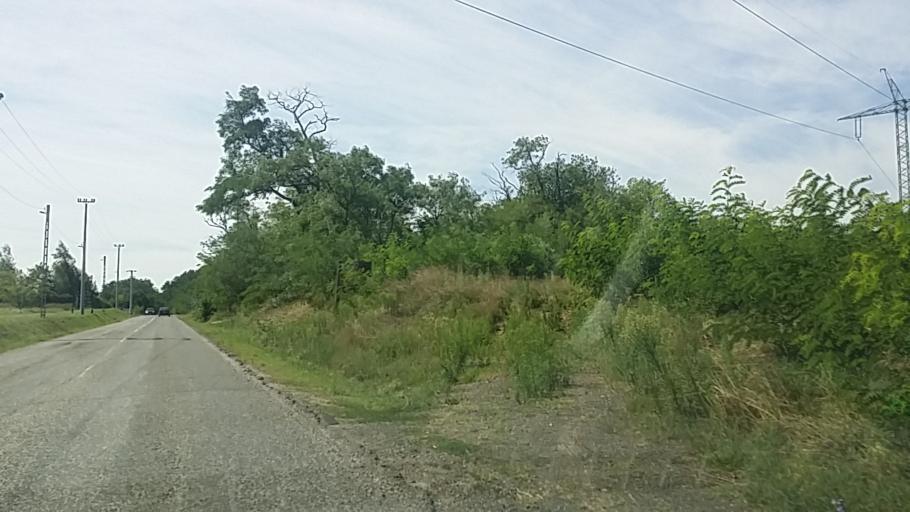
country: HU
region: Pest
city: Szada
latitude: 47.6213
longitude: 19.3010
